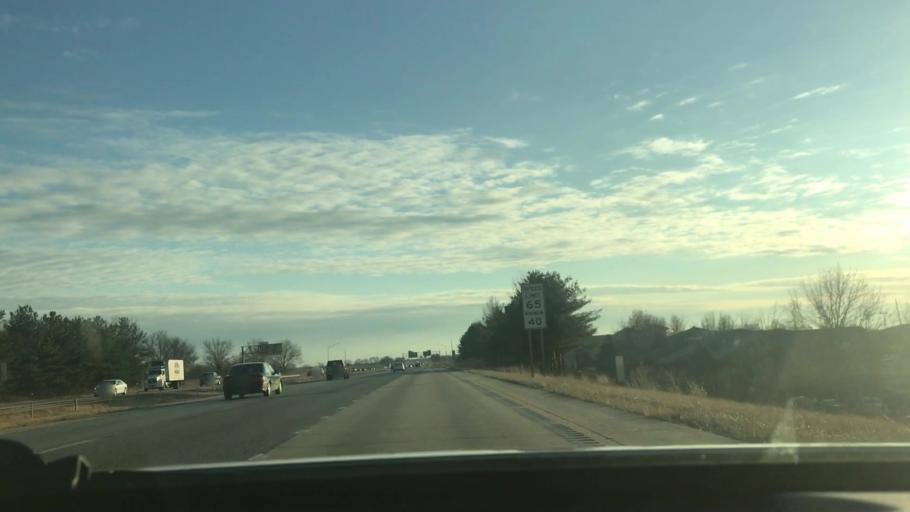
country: US
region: Missouri
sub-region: Jackson County
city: Lees Summit
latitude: 38.9752
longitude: -94.3574
